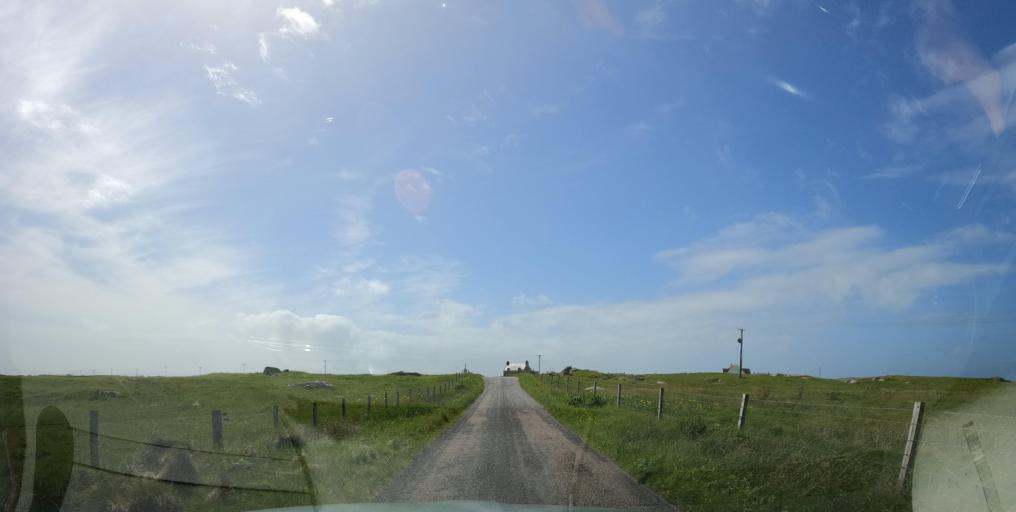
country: GB
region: Scotland
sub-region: Eilean Siar
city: Isle of South Uist
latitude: 57.1660
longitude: -7.3773
